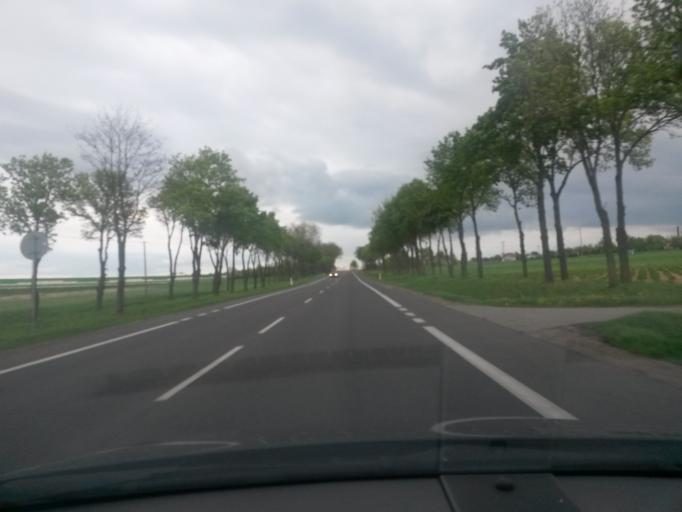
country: PL
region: Masovian Voivodeship
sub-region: Powiat plonski
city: Plonsk
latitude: 52.6038
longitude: 20.3980
